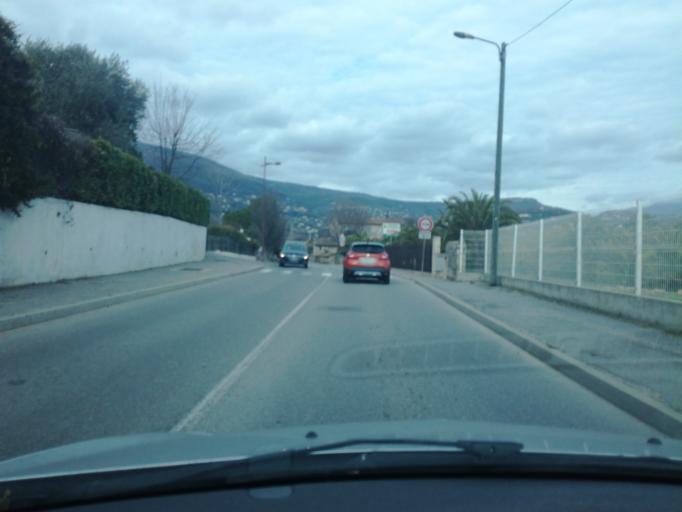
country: FR
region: Provence-Alpes-Cote d'Azur
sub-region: Departement des Alpes-Maritimes
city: Grasse
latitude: 43.6473
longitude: 6.9450
